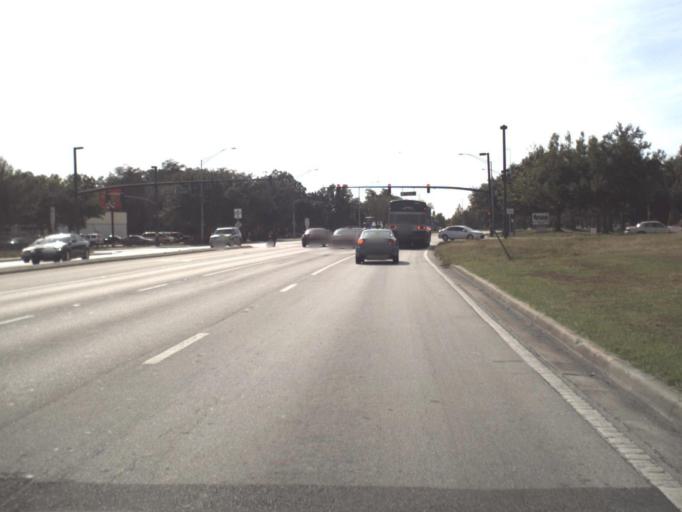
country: US
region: Florida
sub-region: Orange County
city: Orlando
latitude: 28.5409
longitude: -81.4137
